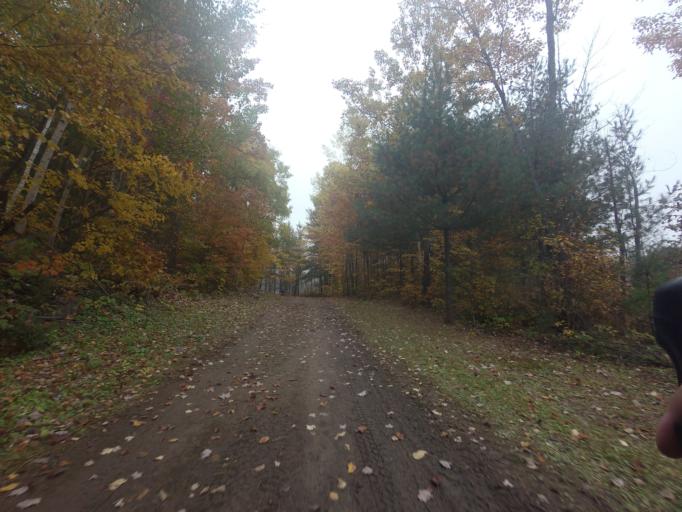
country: CA
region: Ontario
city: Petawawa
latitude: 45.7531
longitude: -77.3605
